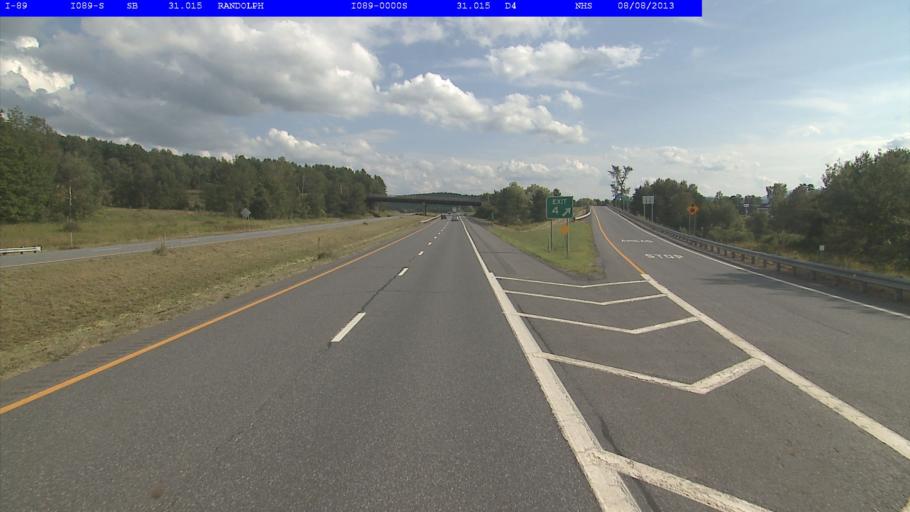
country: US
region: Vermont
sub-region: Orange County
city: Randolph
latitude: 43.9471
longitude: -72.6221
